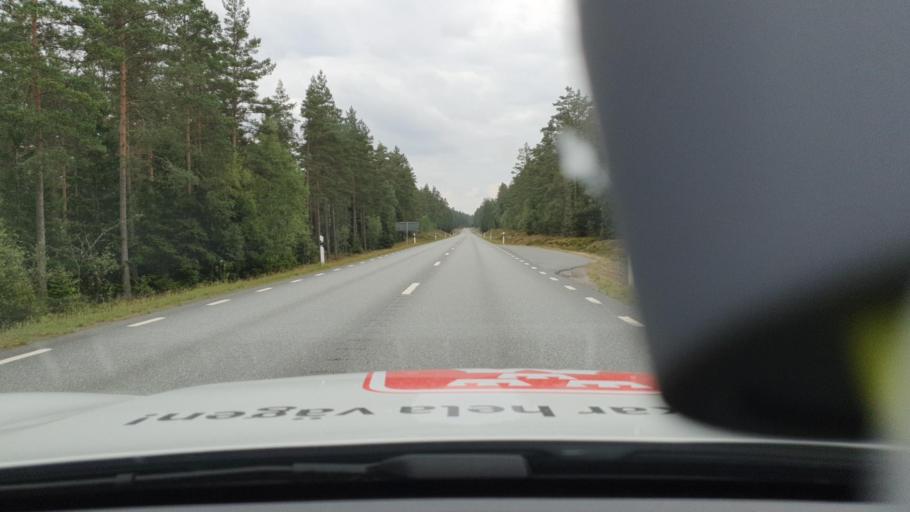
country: SE
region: Joenkoeping
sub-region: Gislaveds Kommun
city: Gislaved
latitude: 57.4148
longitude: 13.6008
